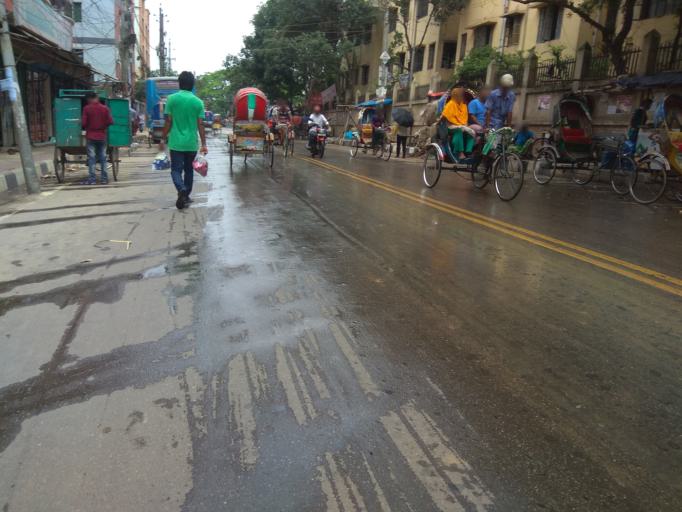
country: BD
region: Dhaka
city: Tungi
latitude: 23.8243
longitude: 90.3590
